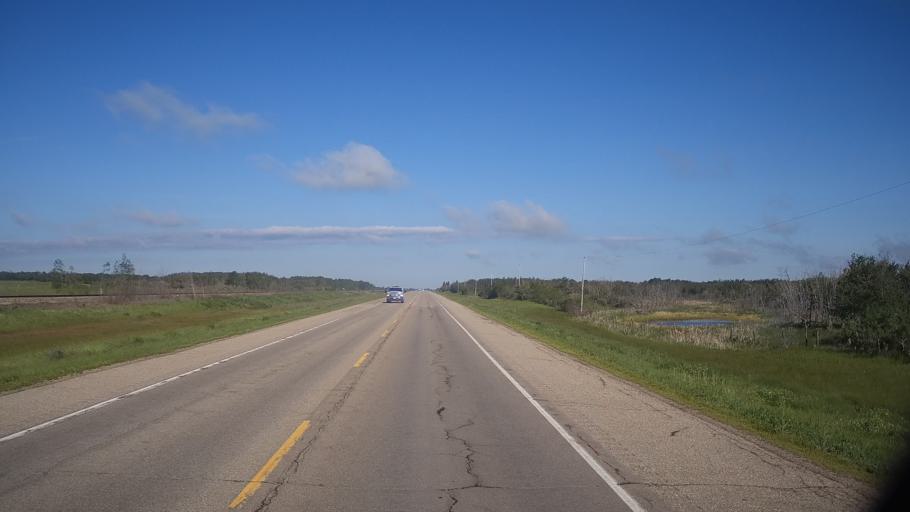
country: CA
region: Saskatchewan
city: Lanigan
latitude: 51.8545
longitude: -105.0831
